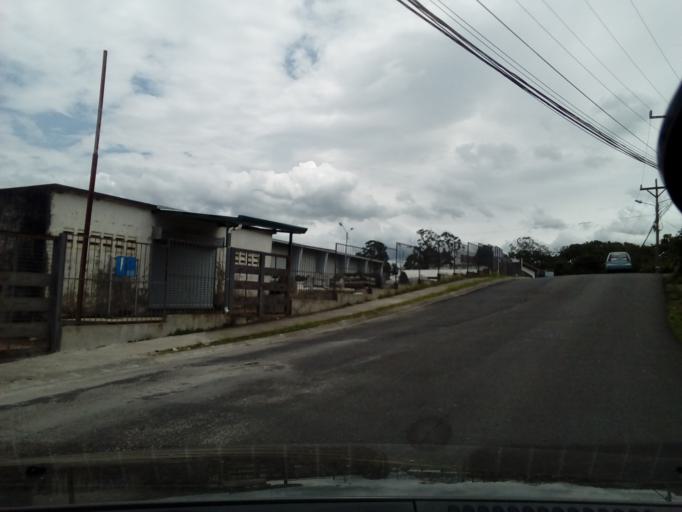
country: CR
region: Heredia
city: San Josecito
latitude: 10.0155
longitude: -84.1080
